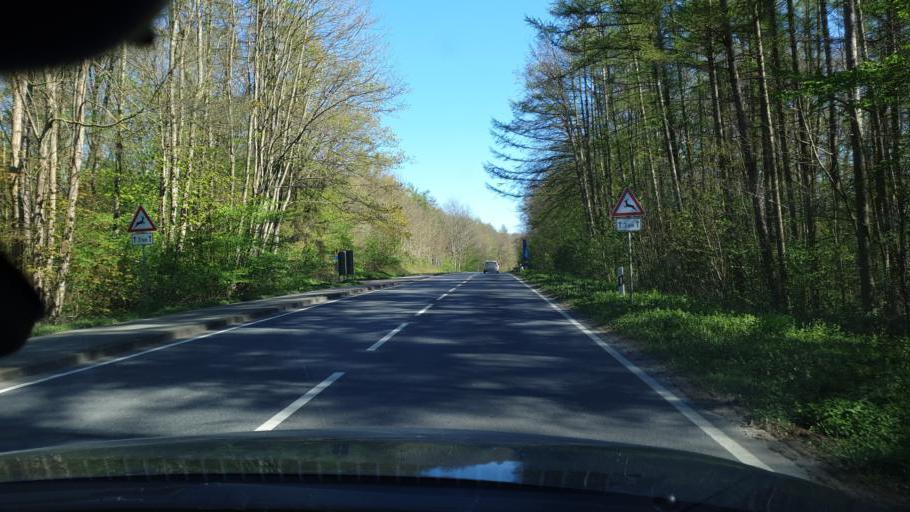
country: DE
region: Mecklenburg-Vorpommern
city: Werdervorstadt
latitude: 53.6507
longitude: 11.4316
